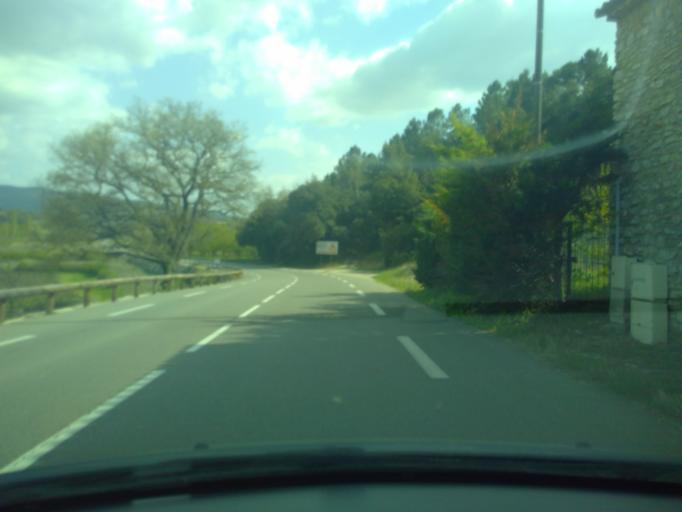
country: FR
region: Provence-Alpes-Cote d'Azur
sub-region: Departement du Vaucluse
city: Malaucene
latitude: 44.2050
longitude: 5.1065
